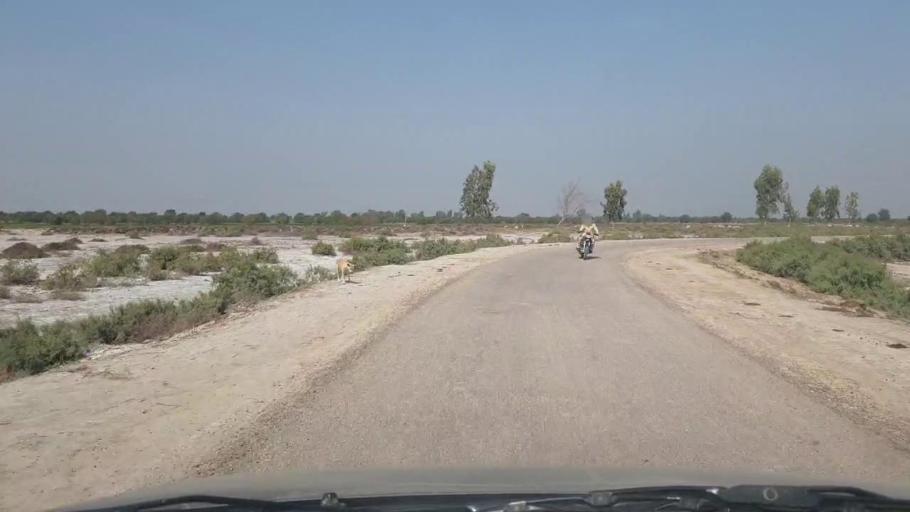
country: PK
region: Sindh
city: Mirwah Gorchani
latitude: 25.3359
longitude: 69.1467
